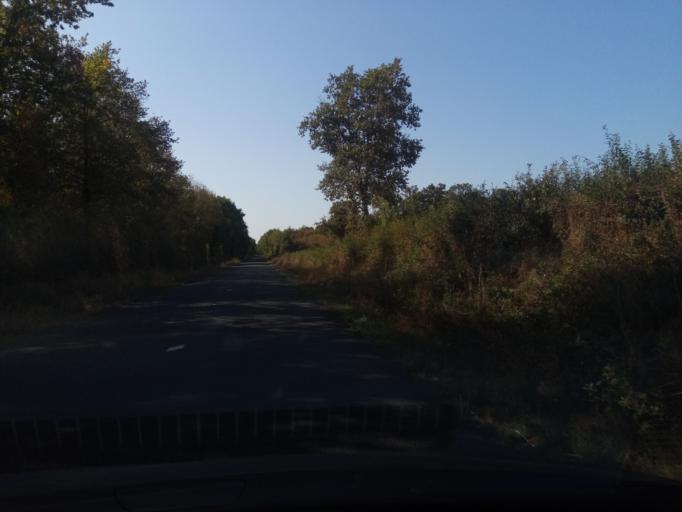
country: FR
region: Poitou-Charentes
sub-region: Departement de la Vienne
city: Saulge
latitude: 46.3502
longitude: 0.8714
